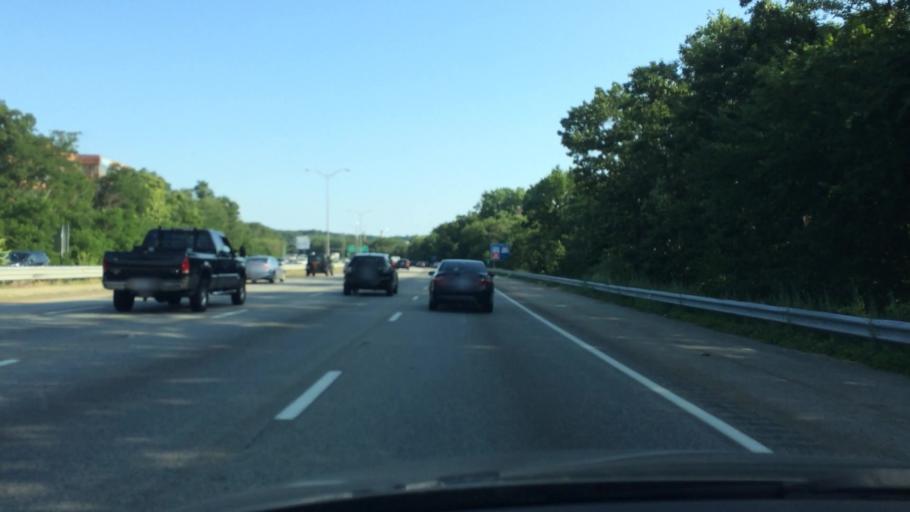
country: US
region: Massachusetts
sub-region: Middlesex County
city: Stoneham
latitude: 42.4880
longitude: -71.1179
